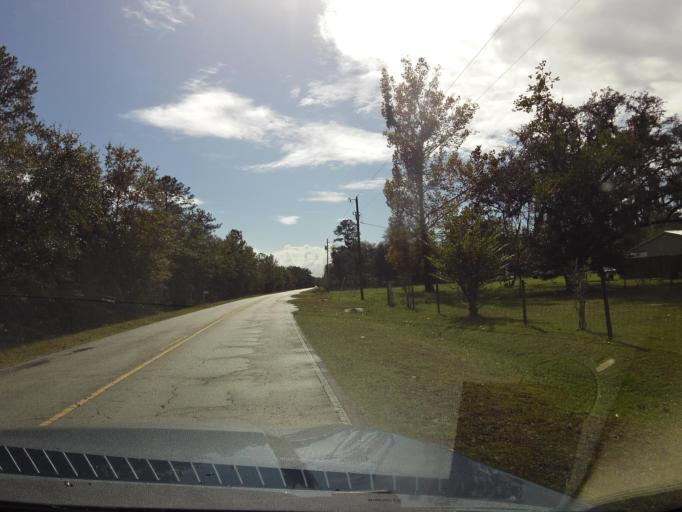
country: US
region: Florida
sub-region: Clay County
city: Asbury Lake
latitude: 29.9891
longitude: -81.8397
